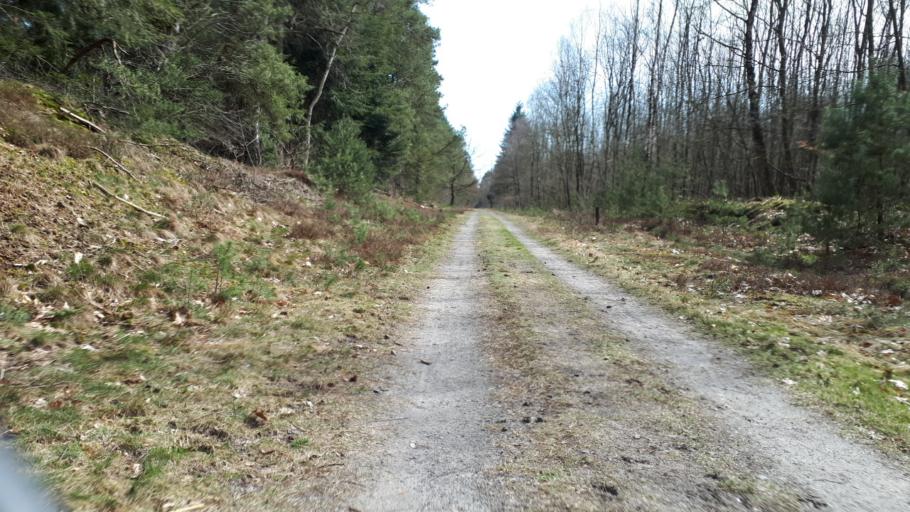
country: DE
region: Lower Saxony
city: Grossenkneten
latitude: 53.0251
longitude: 8.2914
